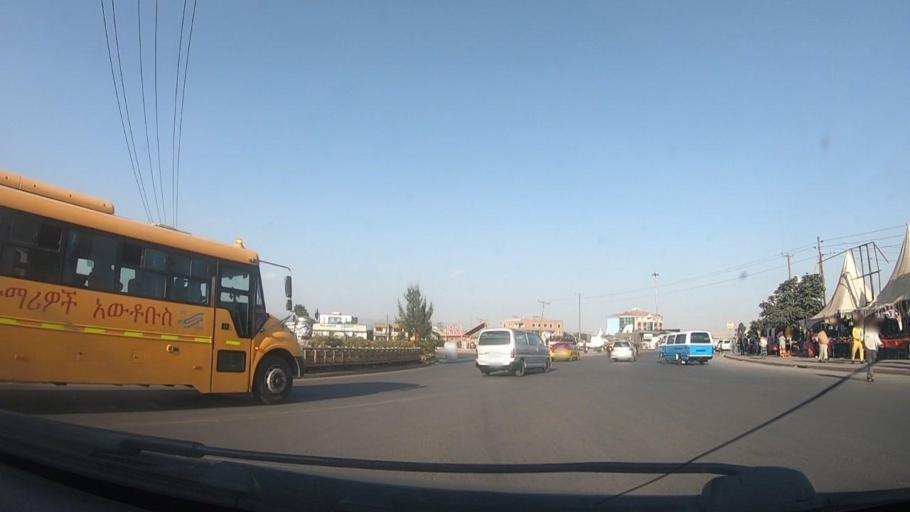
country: ET
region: Adis Abeba
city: Addis Ababa
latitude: 8.9365
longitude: 38.7347
